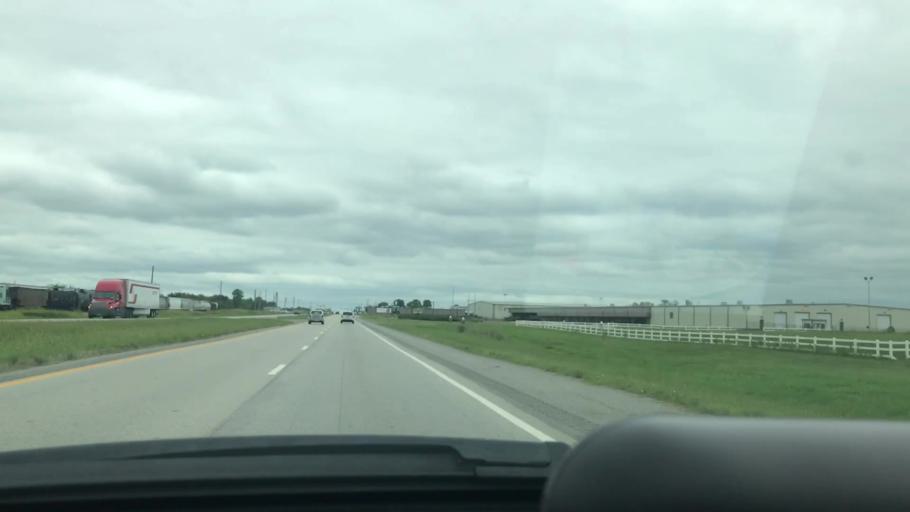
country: US
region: Oklahoma
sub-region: Mayes County
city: Chouteau
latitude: 36.2378
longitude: -95.3380
